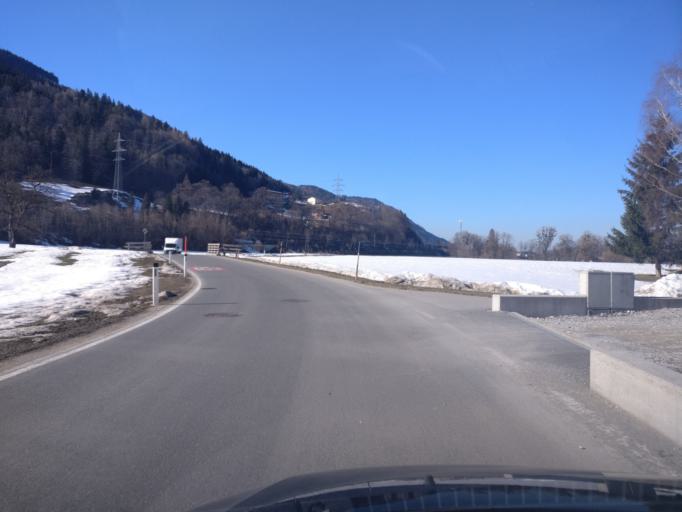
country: AT
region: Salzburg
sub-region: Politischer Bezirk Hallein
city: Kuchl
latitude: 47.6167
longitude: 13.1418
